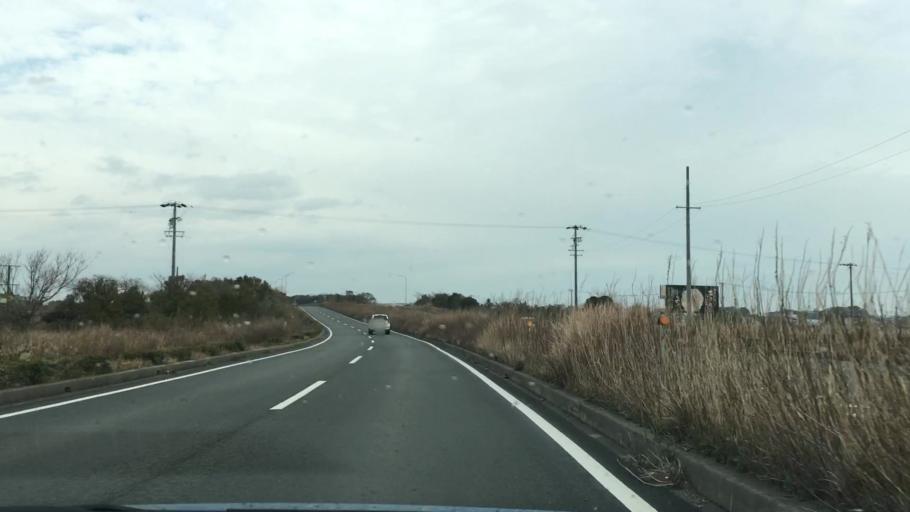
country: JP
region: Aichi
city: Tahara
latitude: 34.6916
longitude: 137.3201
